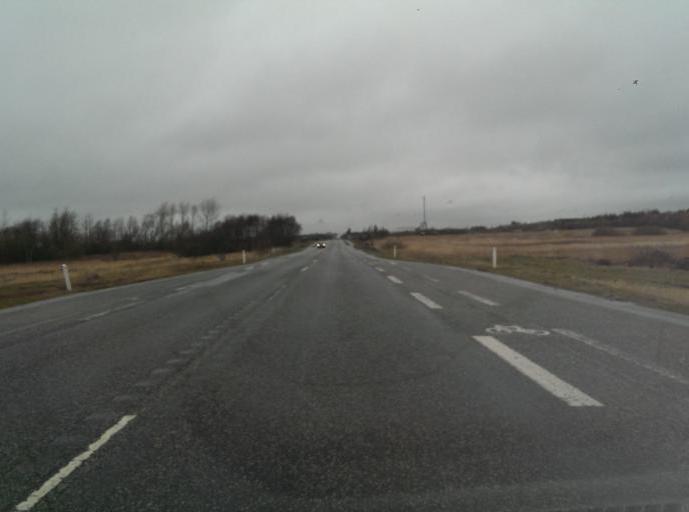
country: DK
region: Central Jutland
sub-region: Ringkobing-Skjern Kommune
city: Ringkobing
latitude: 56.1348
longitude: 8.2812
